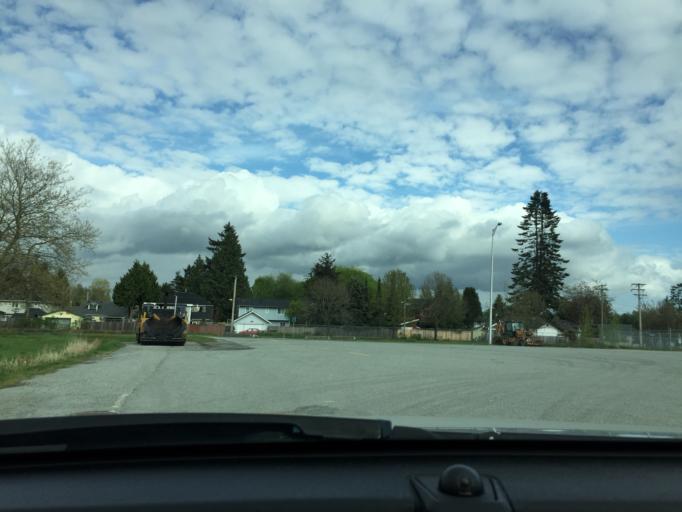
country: CA
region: British Columbia
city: Richmond
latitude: 49.1889
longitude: -123.1519
